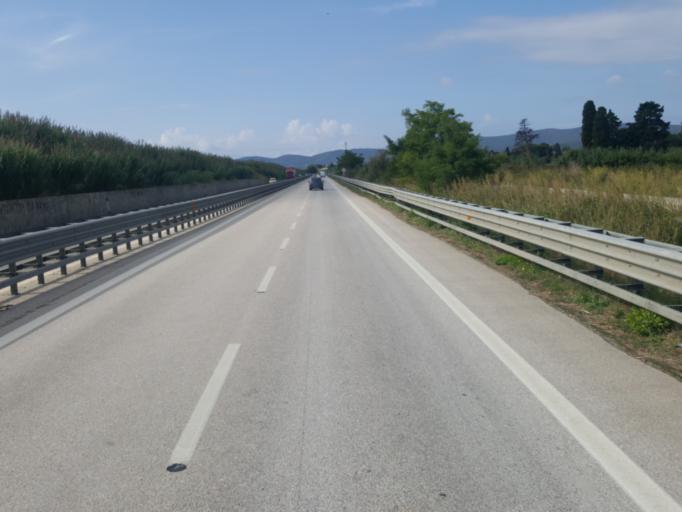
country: IT
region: Tuscany
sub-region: Provincia di Livorno
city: Venturina
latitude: 42.9953
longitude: 10.5770
